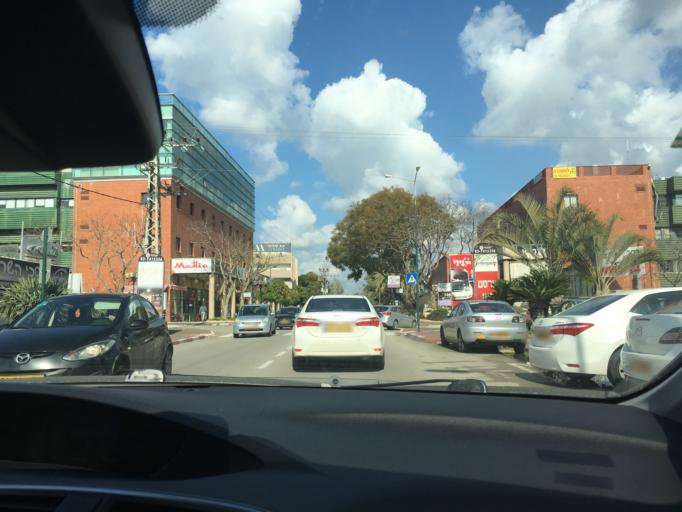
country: IL
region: Central District
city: Kfar Saba
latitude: 32.1765
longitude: 34.9272
